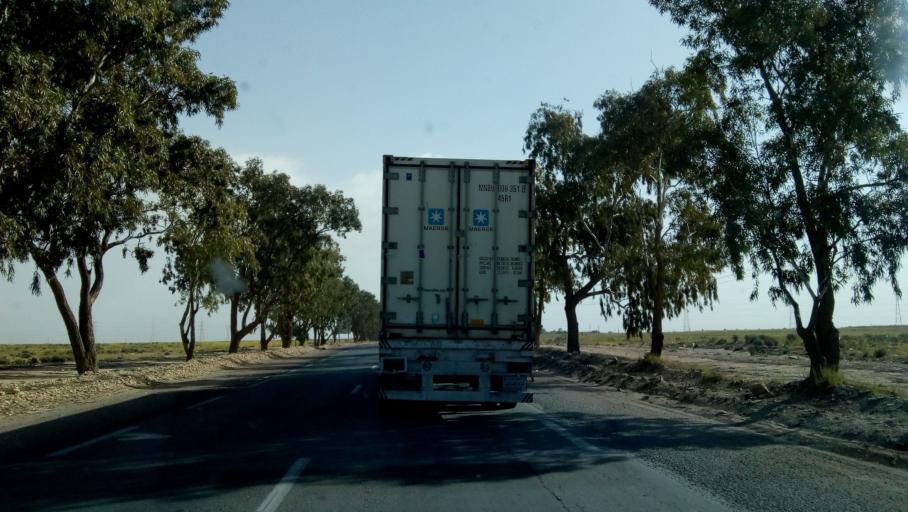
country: TN
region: Qabis
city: Gabes
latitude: 33.8895
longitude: 10.0265
